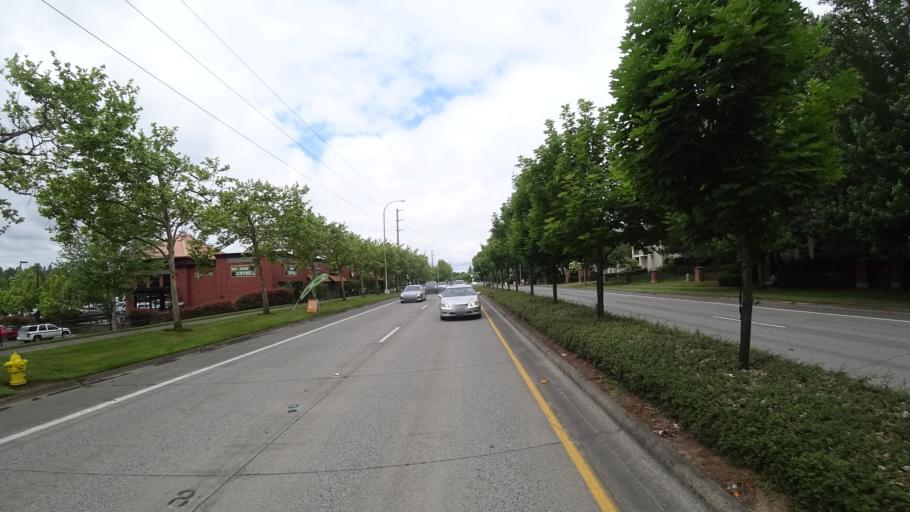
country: US
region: Oregon
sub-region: Washington County
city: Rockcreek
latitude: 45.5365
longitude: -122.8828
